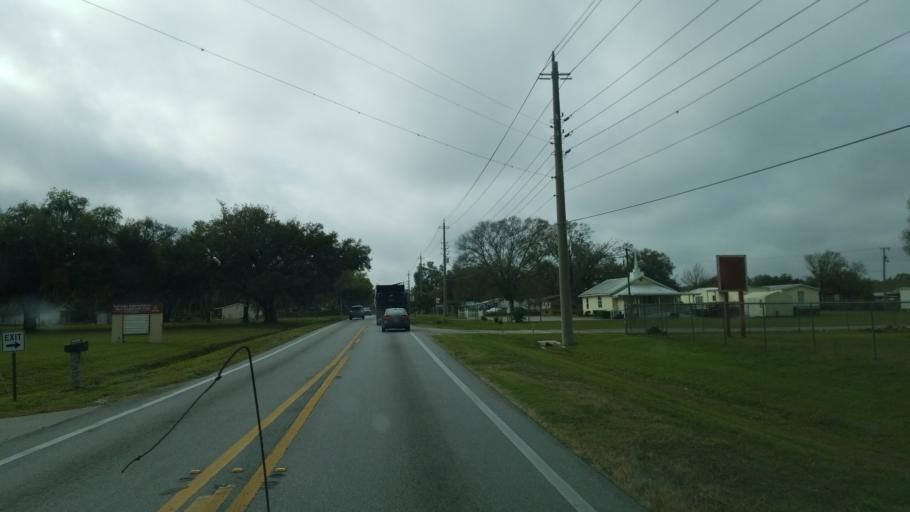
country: US
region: Florida
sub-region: Polk County
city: Kathleen
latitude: 28.0786
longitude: -82.0067
